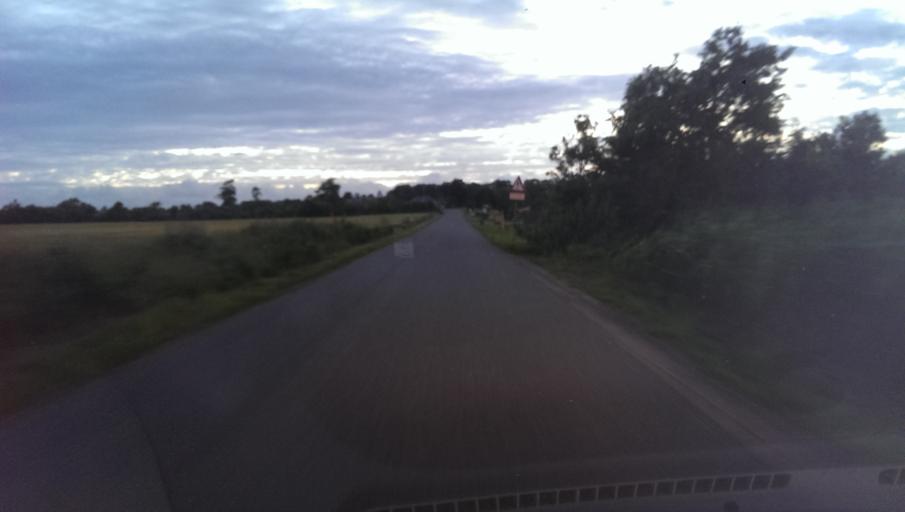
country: DK
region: South Denmark
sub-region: Esbjerg Kommune
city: Esbjerg
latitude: 55.5309
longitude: 8.4868
